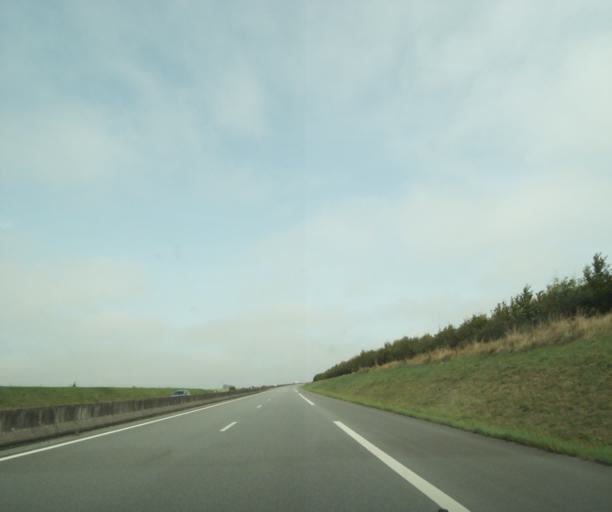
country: FR
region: Lower Normandy
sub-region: Departement de l'Orne
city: Sees
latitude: 48.6114
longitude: 0.1946
